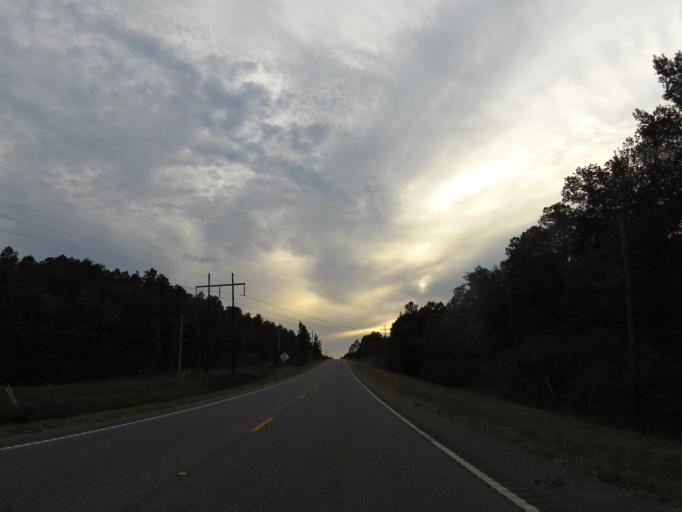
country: US
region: Alabama
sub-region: Escambia County
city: Atmore
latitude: 30.9997
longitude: -87.6011
